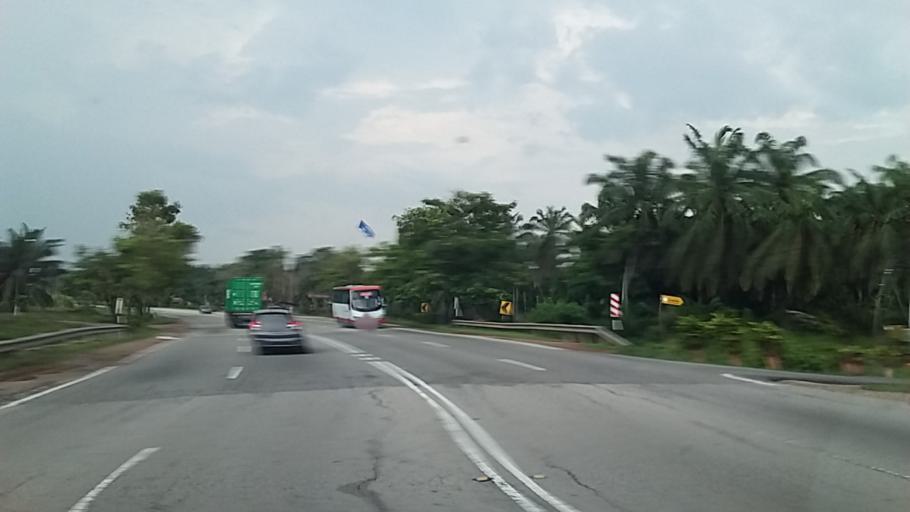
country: MY
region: Johor
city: Parit Raja
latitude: 1.8751
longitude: 103.1409
